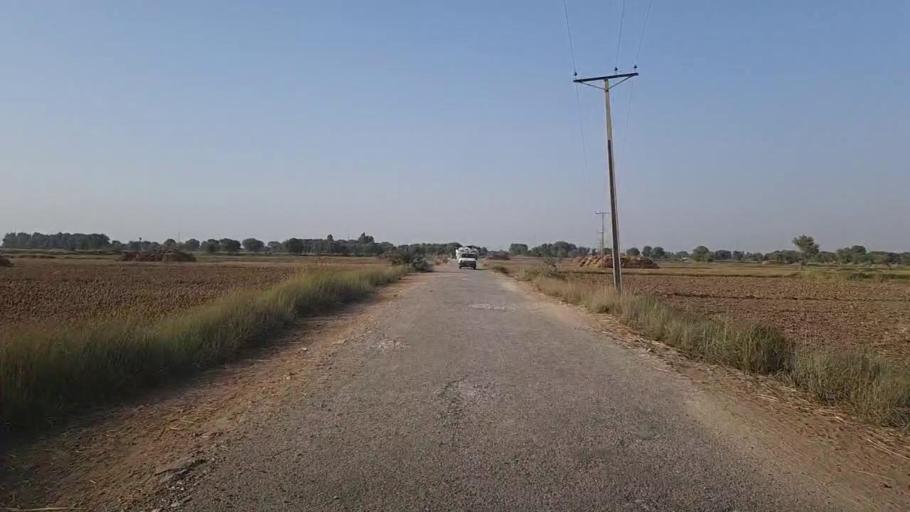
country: PK
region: Sindh
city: Kashmor
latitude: 28.4188
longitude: 69.4095
